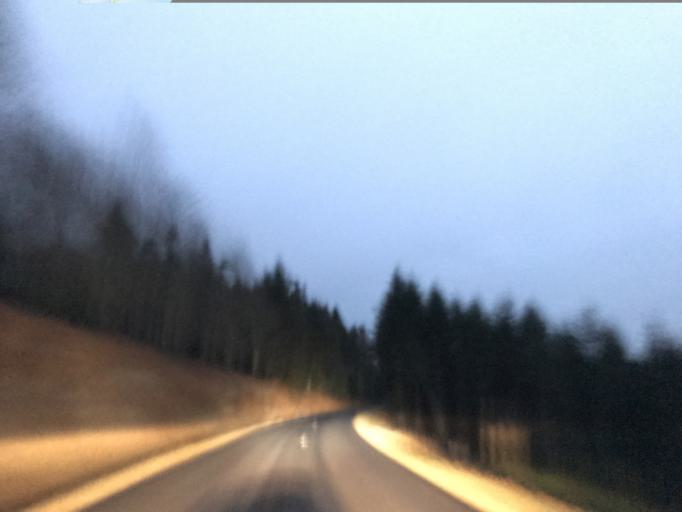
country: FR
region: Auvergne
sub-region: Departement du Puy-de-Dome
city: Celles-sur-Durolle
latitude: 45.7866
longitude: 3.6646
